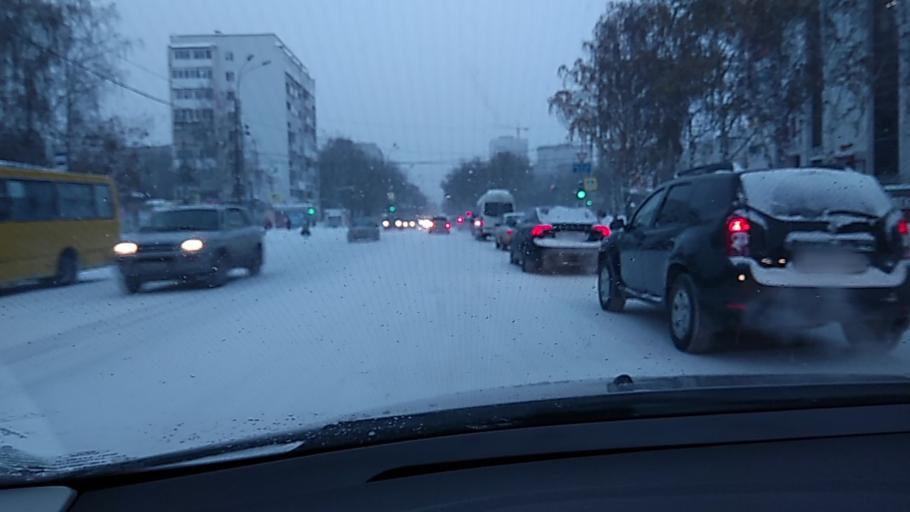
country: RU
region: Sverdlovsk
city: Sovkhoznyy
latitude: 56.8174
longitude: 60.5625
